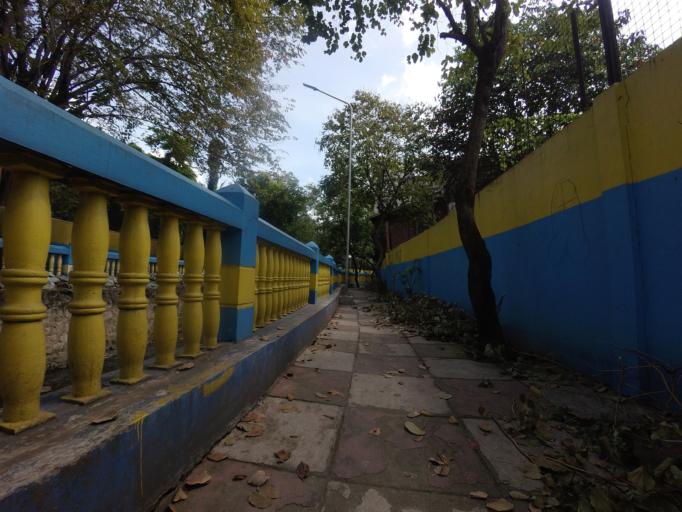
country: PH
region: Calabarzon
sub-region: Province of Rizal
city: Pateros
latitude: 14.5647
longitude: 121.0876
